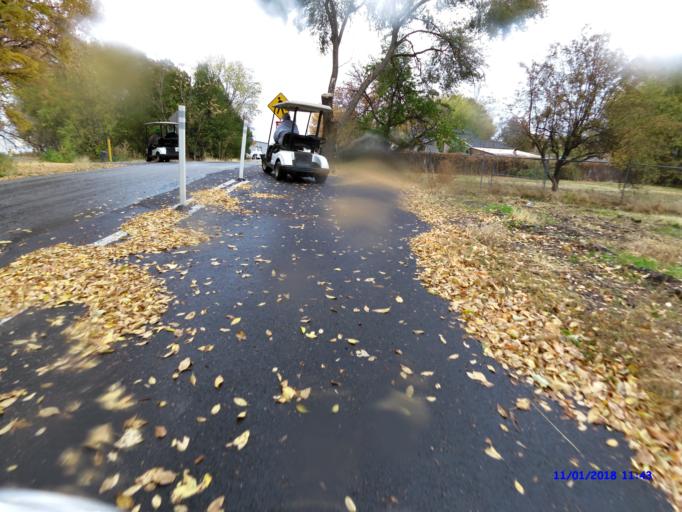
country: US
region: Utah
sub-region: Weber County
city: Ogden
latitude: 41.2355
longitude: -111.9860
